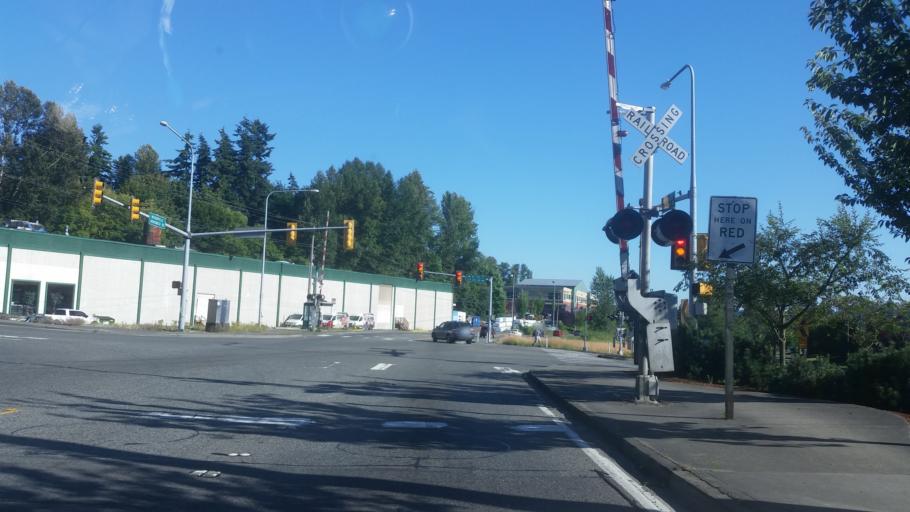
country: US
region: Washington
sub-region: King County
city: Woodinville
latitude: 47.7657
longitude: -122.1544
